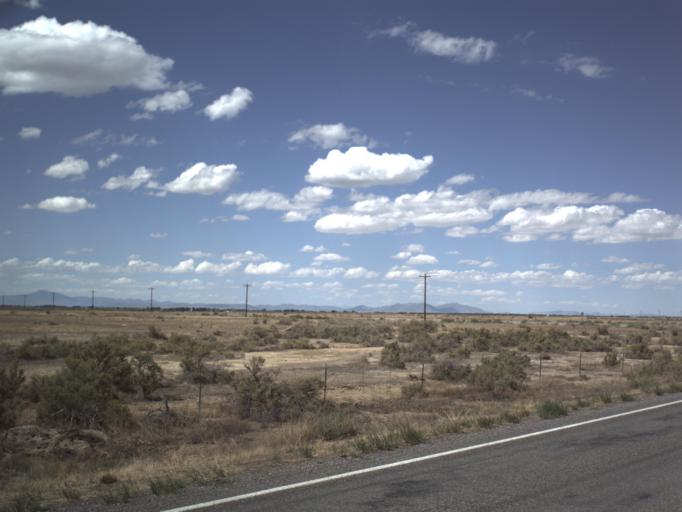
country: US
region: Utah
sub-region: Millard County
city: Delta
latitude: 39.2858
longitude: -112.4632
